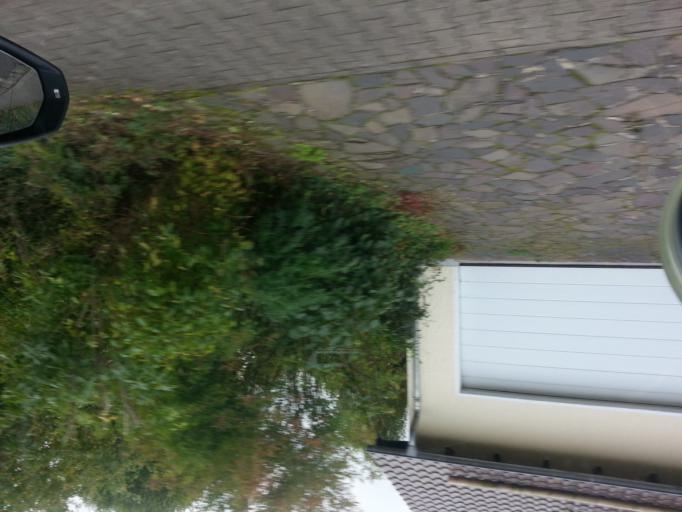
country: DE
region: Saarland
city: Freisen
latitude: 49.5458
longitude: 7.2477
